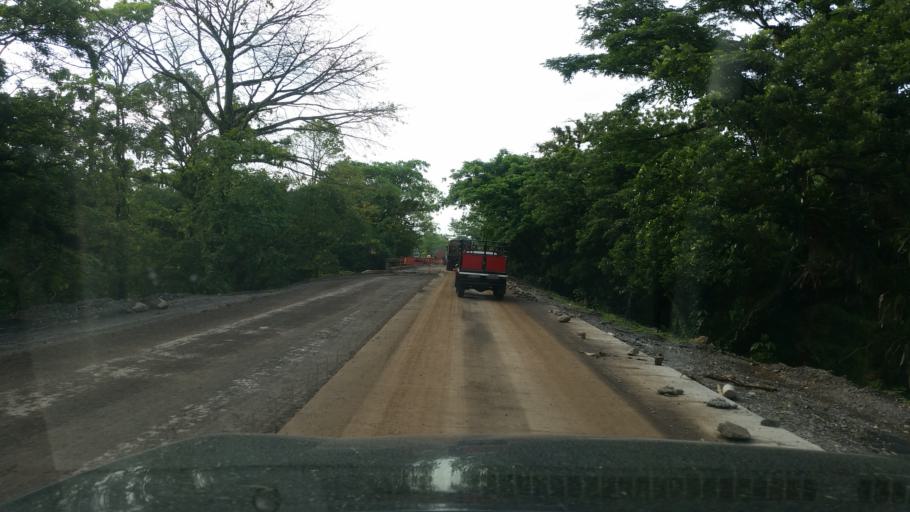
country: NI
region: Matagalpa
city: Rio Blanco
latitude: 13.0803
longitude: -85.0602
